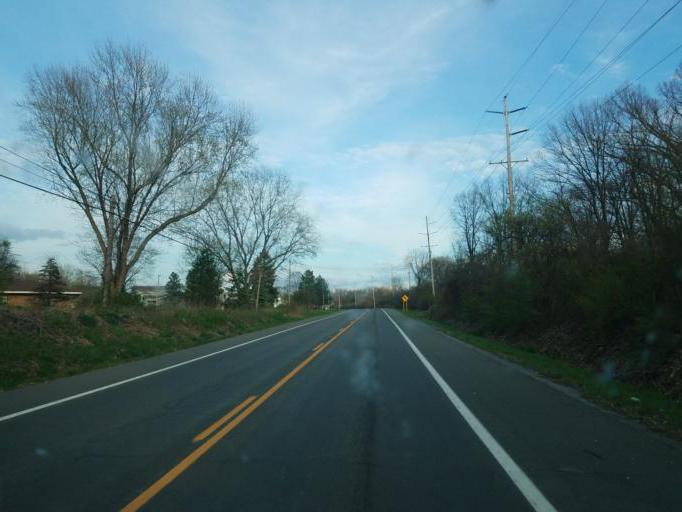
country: US
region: Ohio
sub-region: Erie County
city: Huron
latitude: 41.3816
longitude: -82.5123
